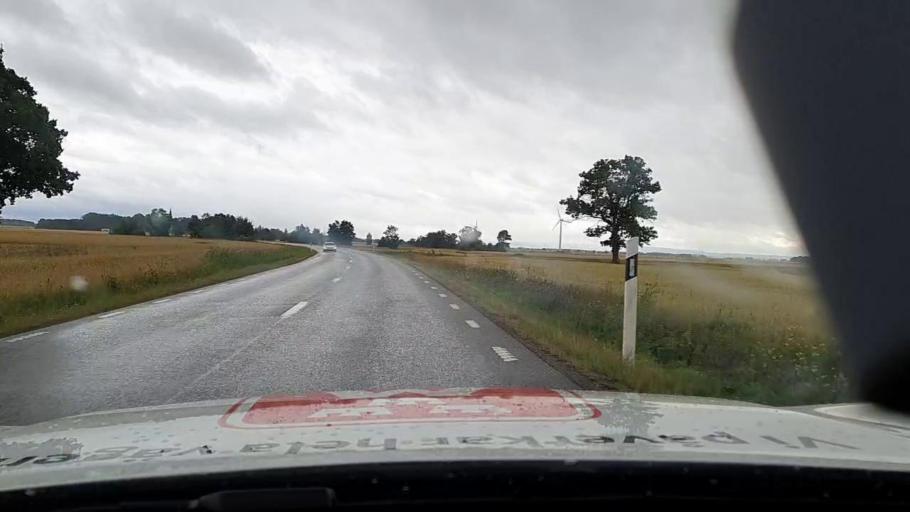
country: SE
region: Vaestra Goetaland
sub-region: Toreboda Kommun
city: Toereboda
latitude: 58.6170
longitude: 14.0116
